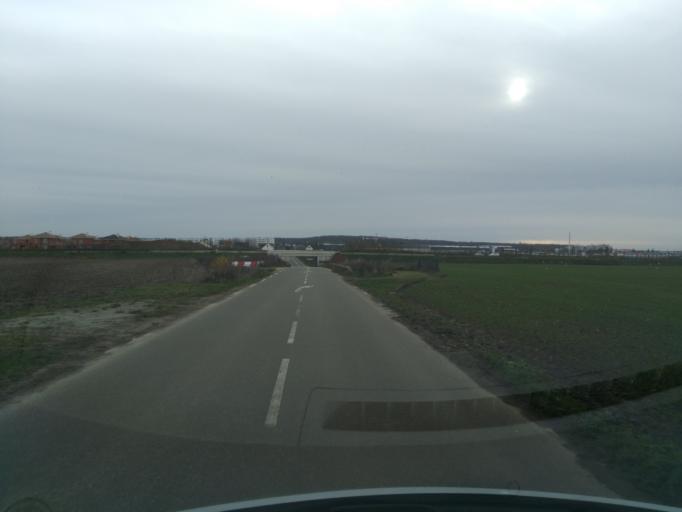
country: FR
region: Ile-de-France
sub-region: Departement des Yvelines
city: Les Clayes-sous-Bois
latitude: 48.8363
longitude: 1.9839
